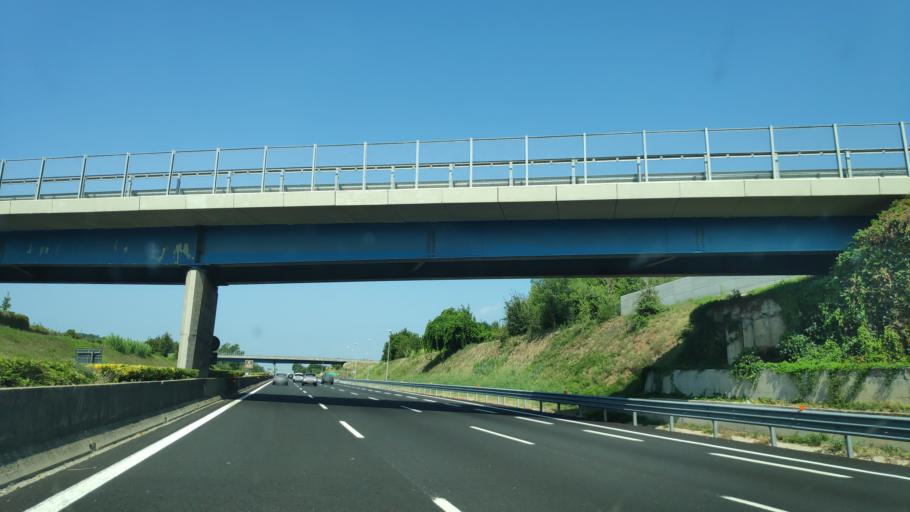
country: IT
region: Campania
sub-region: Provincia di Caserta
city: Bivio Mortola
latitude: 41.4315
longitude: 13.9015
